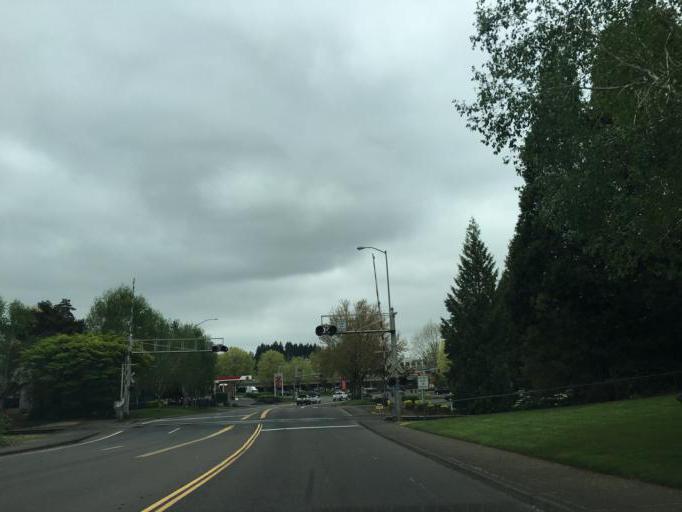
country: US
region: Oregon
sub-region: Washington County
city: Durham
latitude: 45.4061
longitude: -122.7472
